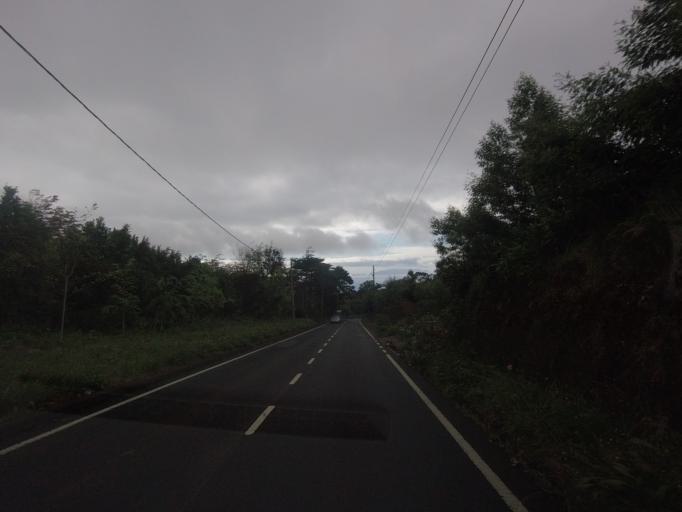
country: PT
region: Madeira
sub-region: Santa Cruz
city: Santa Cruz
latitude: 32.7110
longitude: -16.7938
